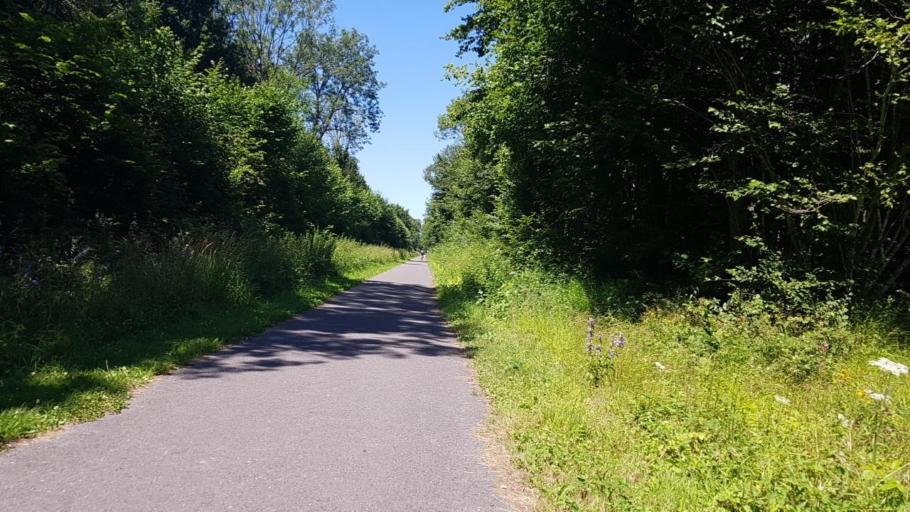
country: BE
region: Wallonia
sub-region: Province du Hainaut
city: Beaumont
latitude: 50.1698
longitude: 4.2401
